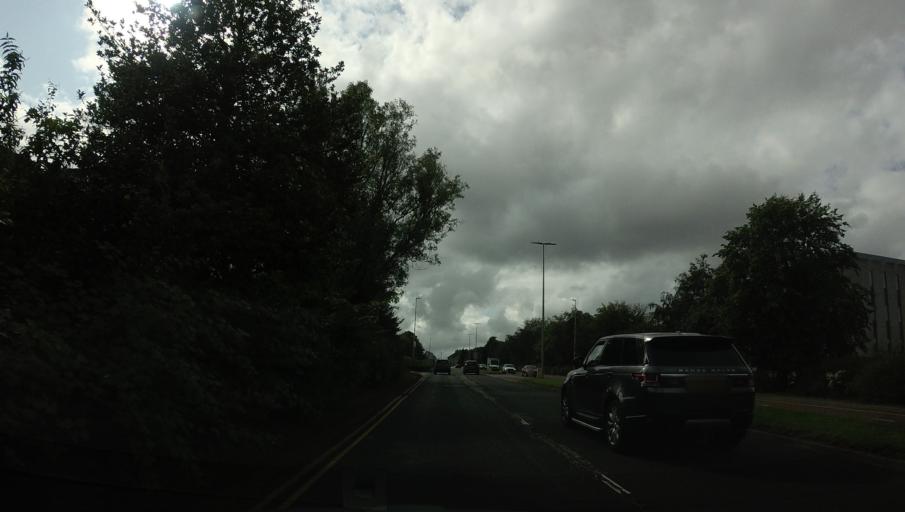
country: GB
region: Scotland
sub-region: Aberdeen City
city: Cults
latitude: 57.1523
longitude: -2.1463
